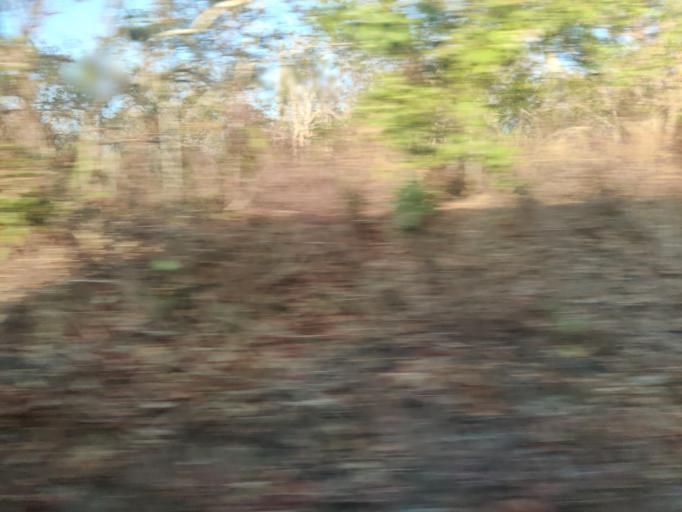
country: CO
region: Atlantico
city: Piojo
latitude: 10.7451
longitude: -75.2442
